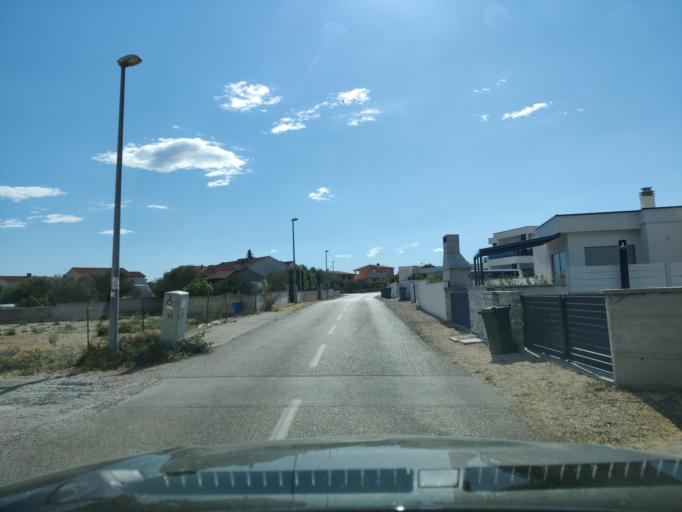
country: HR
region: Sibensko-Kniniska
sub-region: Grad Sibenik
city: Sibenik
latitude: 43.7282
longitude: 15.8430
